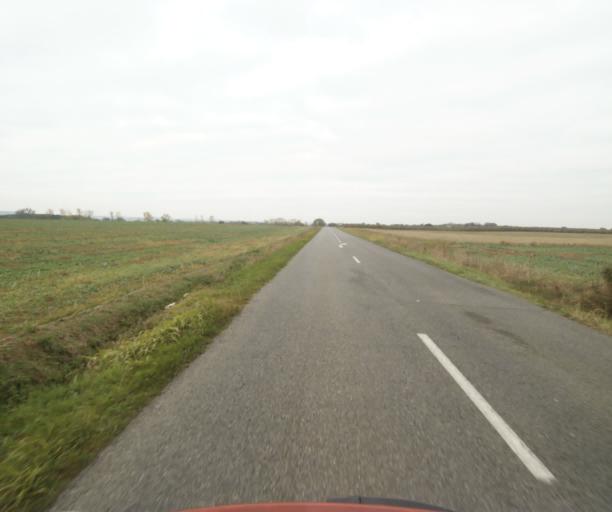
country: FR
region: Midi-Pyrenees
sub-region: Departement du Tarn-et-Garonne
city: Verdun-sur-Garonne
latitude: 43.8153
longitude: 1.1929
